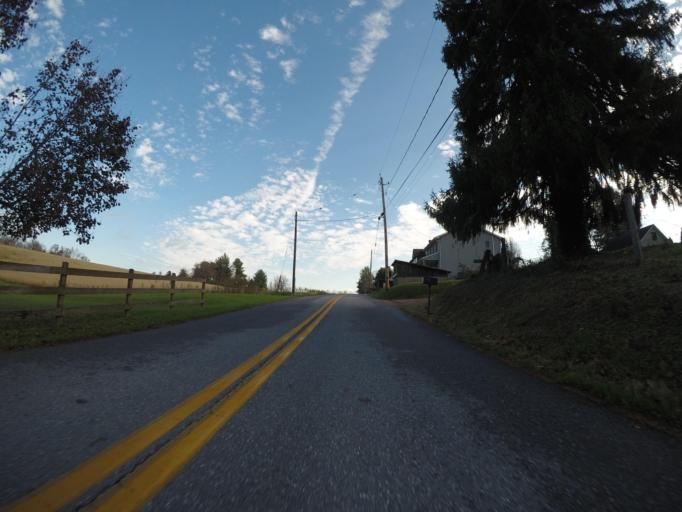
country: US
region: Maryland
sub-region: Carroll County
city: Hampstead
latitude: 39.5798
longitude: -76.8064
